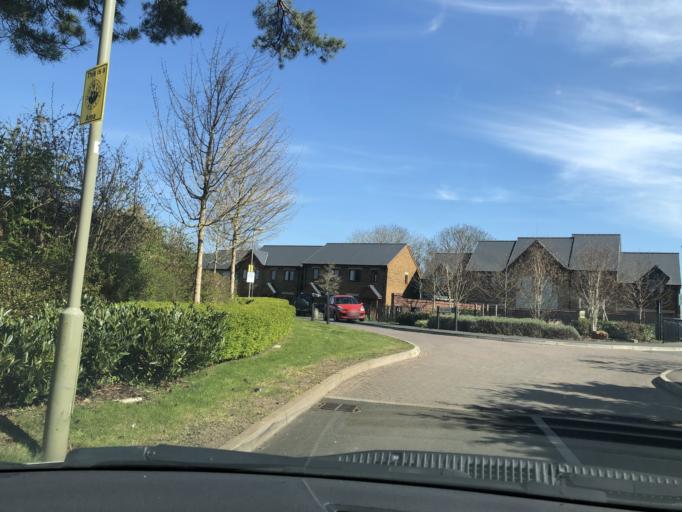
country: GB
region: England
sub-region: Oxfordshire
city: Hook Norton
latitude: 51.9994
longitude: -1.4734
